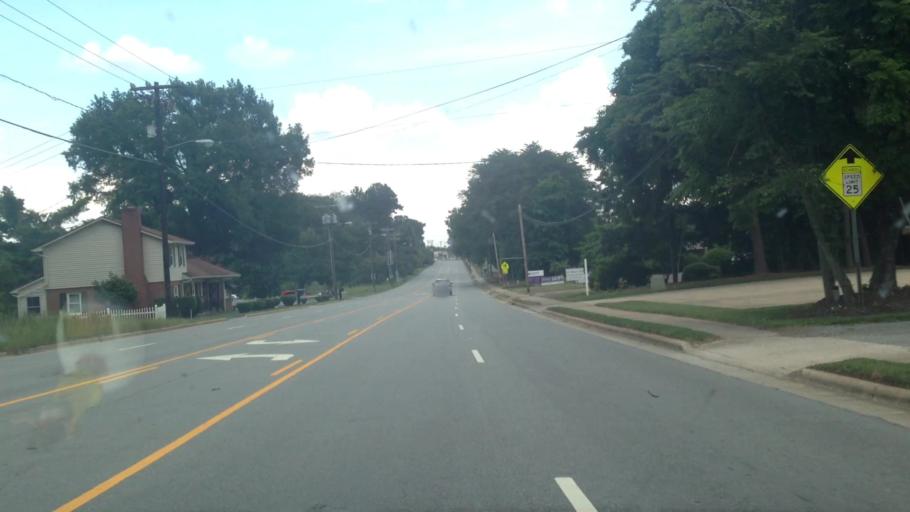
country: US
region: North Carolina
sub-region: Rockingham County
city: Mayodan
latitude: 36.4017
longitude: -79.9748
